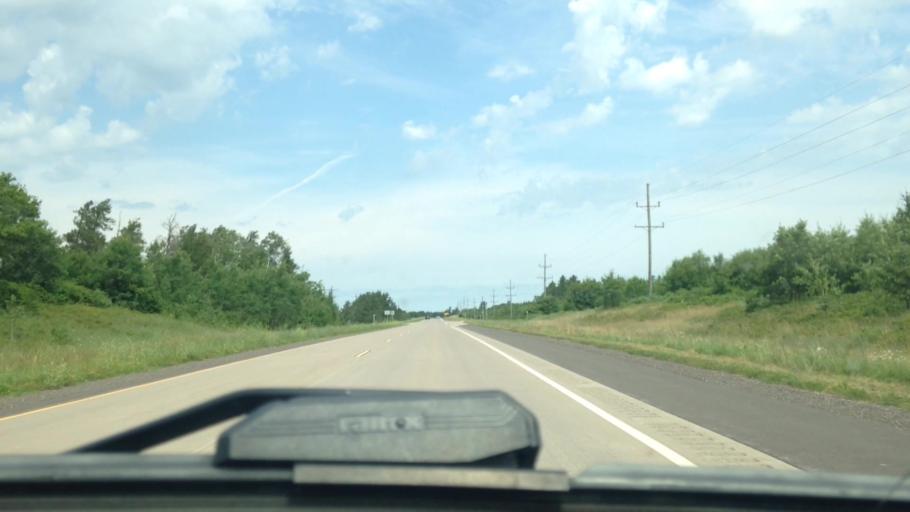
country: US
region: Wisconsin
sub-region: Douglas County
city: Lake Nebagamon
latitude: 46.2766
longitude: -91.8067
